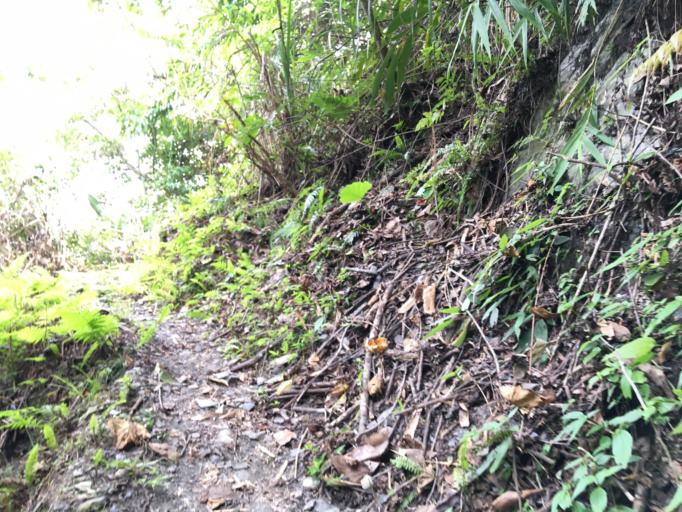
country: TW
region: Taiwan
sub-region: Yilan
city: Yilan
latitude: 24.4249
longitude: 121.7022
